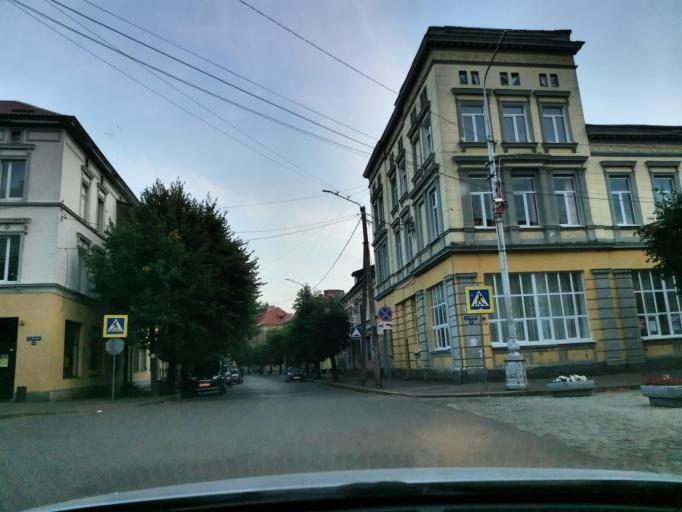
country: RU
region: Kaliningrad
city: Sovetsk
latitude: 55.0808
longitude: 21.8900
